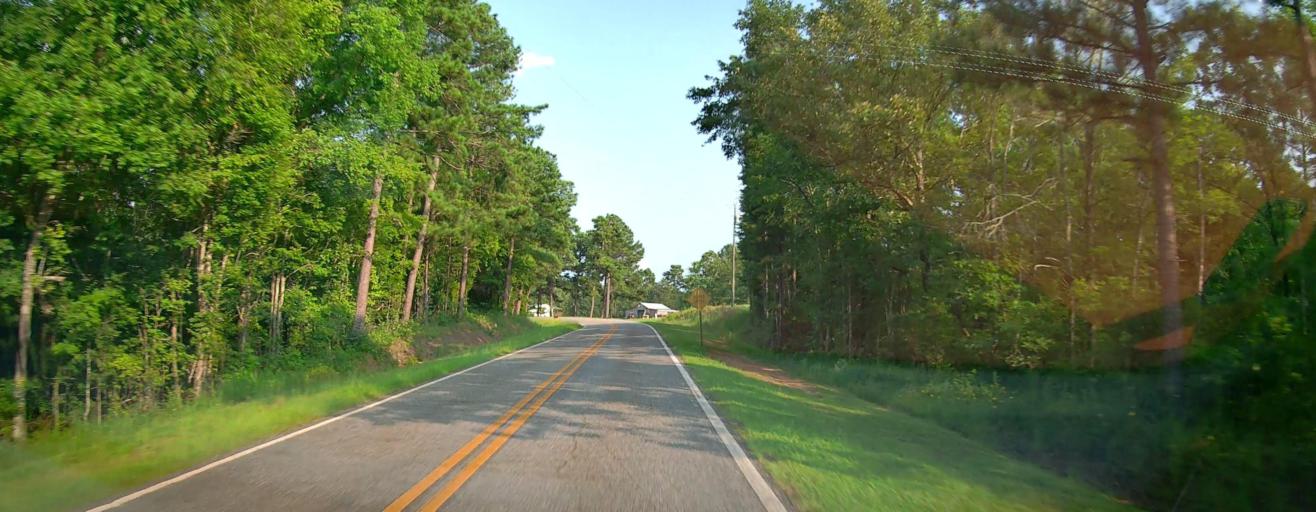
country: US
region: Georgia
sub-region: Monroe County
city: Forsyth
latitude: 33.0946
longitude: -83.7536
